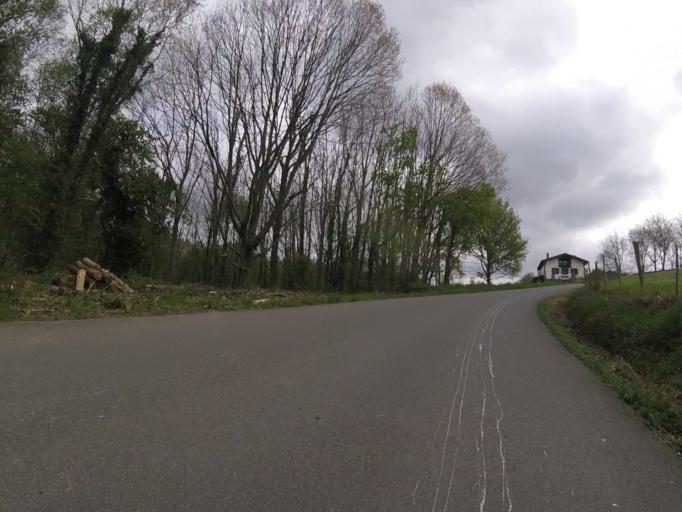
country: ES
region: Basque Country
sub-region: Provincia de Guipuzcoa
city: Zizurkil
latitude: 43.2057
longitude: -2.0773
